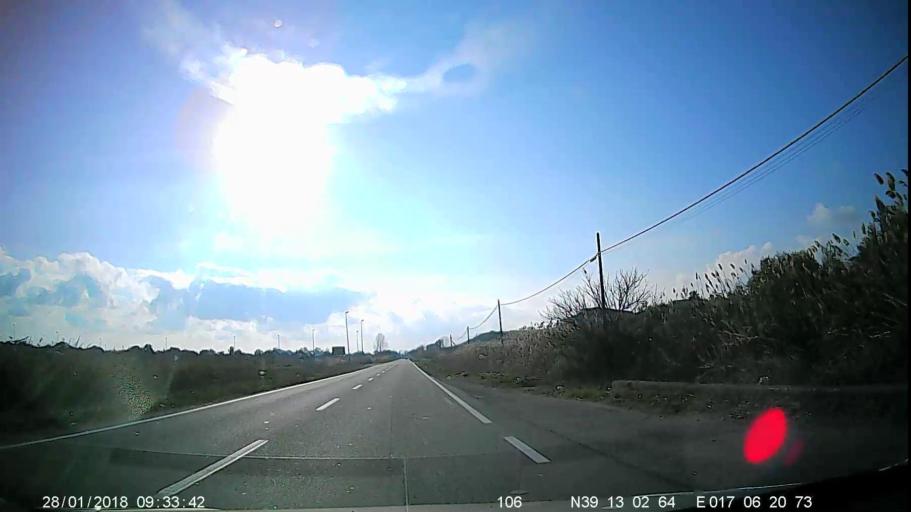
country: IT
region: Calabria
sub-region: Provincia di Crotone
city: Tronca
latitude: 39.2169
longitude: 17.1061
